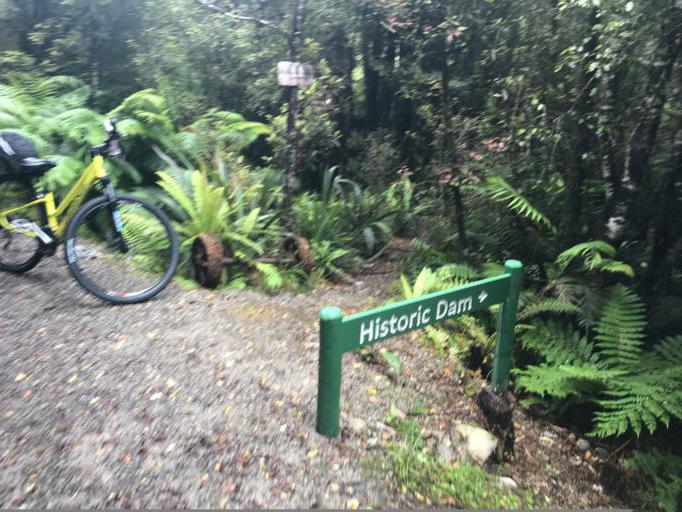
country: NZ
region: West Coast
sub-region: Westland District
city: Hokitika
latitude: -42.7627
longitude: 171.2455
